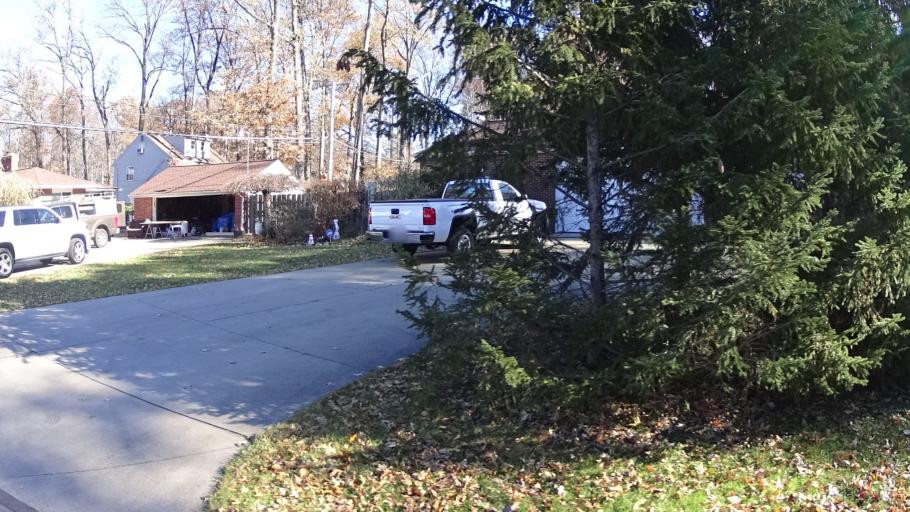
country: US
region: Ohio
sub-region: Lorain County
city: Avon Lake
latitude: 41.5021
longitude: -82.0376
